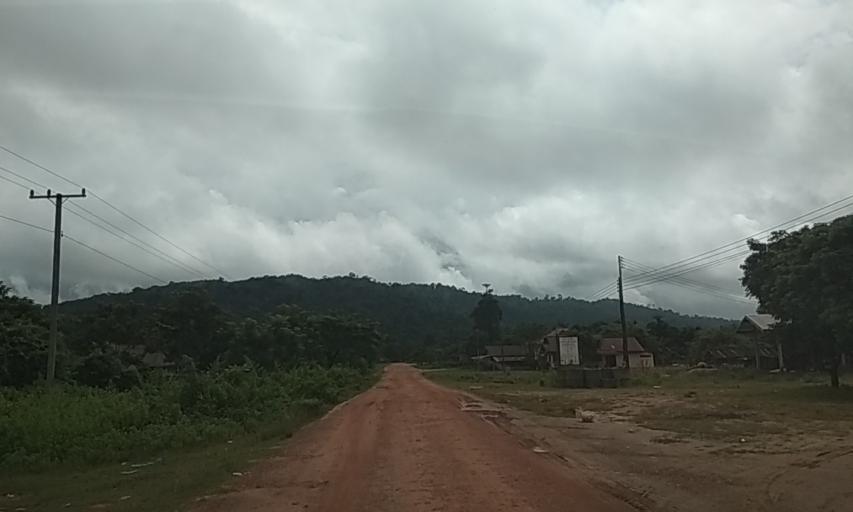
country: LA
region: Bolikhamxai
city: Bolikhan
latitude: 18.5571
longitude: 103.7373
